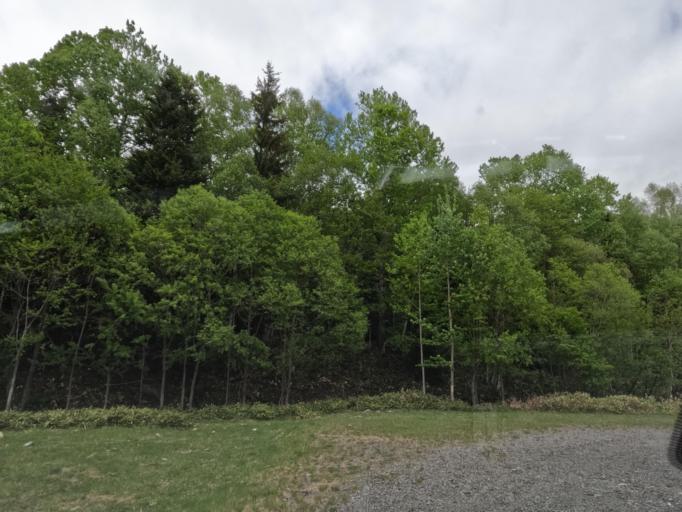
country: JP
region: Hokkaido
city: Kamikawa
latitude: 43.6451
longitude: 143.0236
